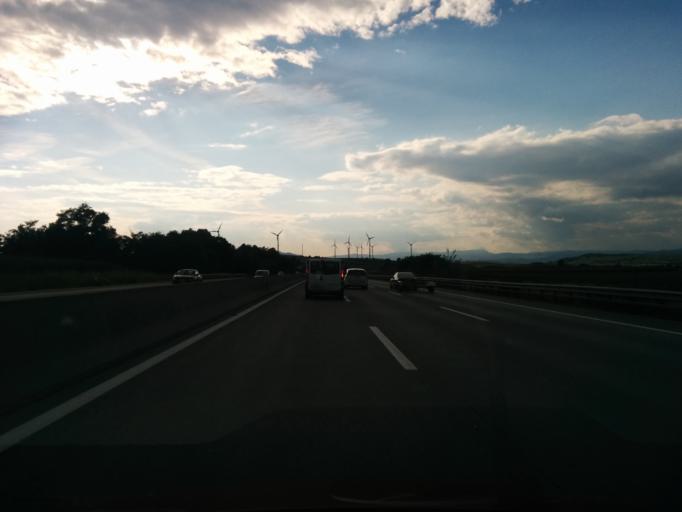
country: AT
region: Lower Austria
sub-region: Politischer Bezirk Sankt Polten
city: Sankt Margarethen an der Sierning
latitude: 48.1687
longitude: 15.4892
